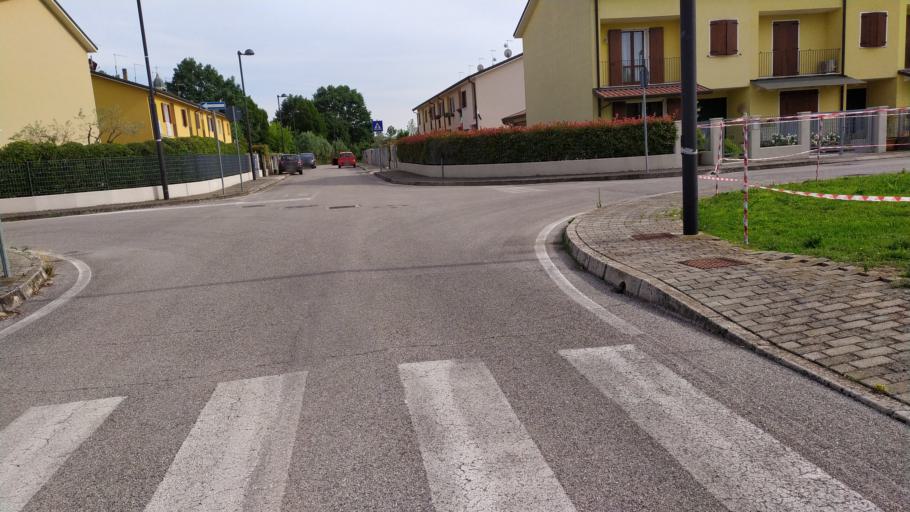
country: IT
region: Veneto
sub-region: Provincia di Padova
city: Villa del Conte
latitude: 45.5902
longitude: 11.8564
